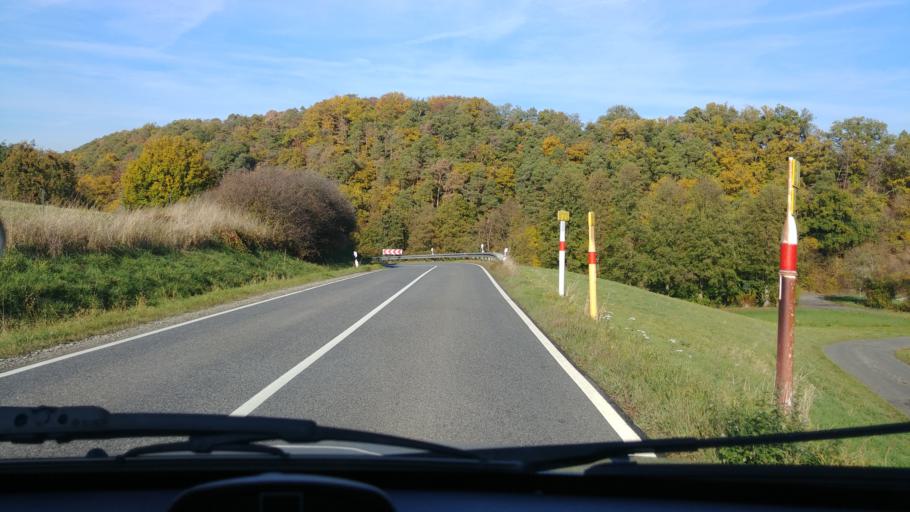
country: DE
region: Hesse
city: Burg Hohenstein
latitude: 50.2139
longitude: 8.0873
